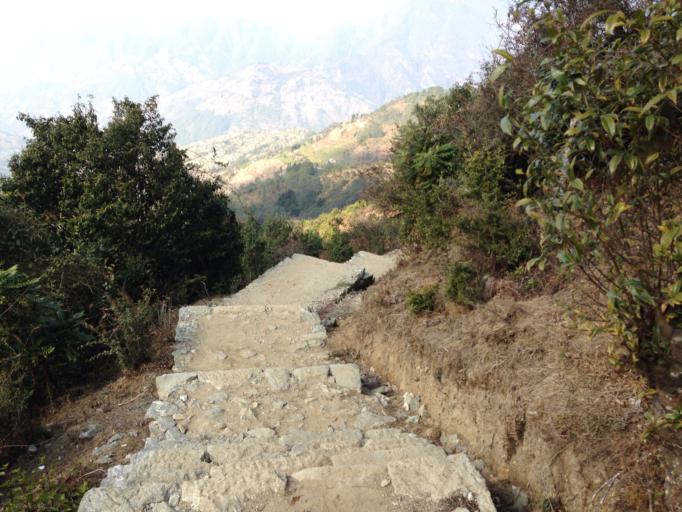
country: NP
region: Central Region
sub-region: Bagmati Zone
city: Nagarkot
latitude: 27.8206
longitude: 85.4466
